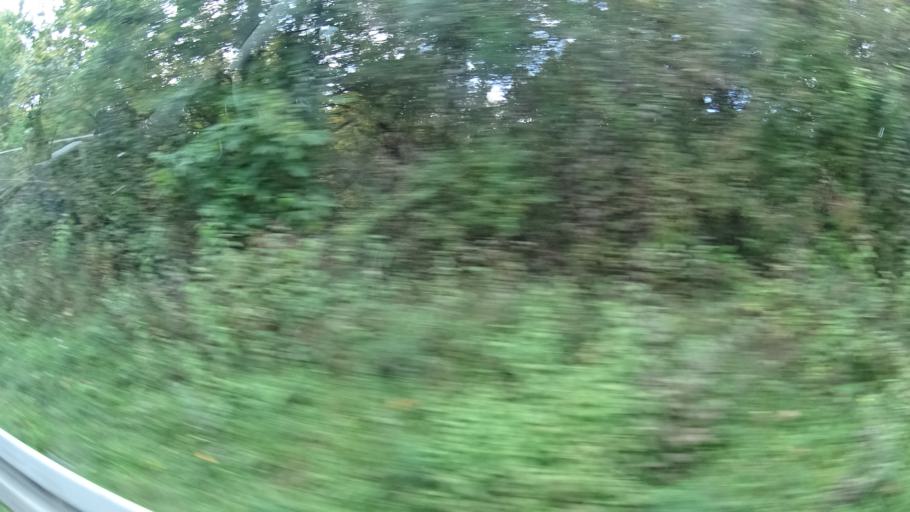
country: DE
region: Bavaria
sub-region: Regierungsbezirk Unterfranken
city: Kitzingen
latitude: 49.7549
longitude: 10.1545
